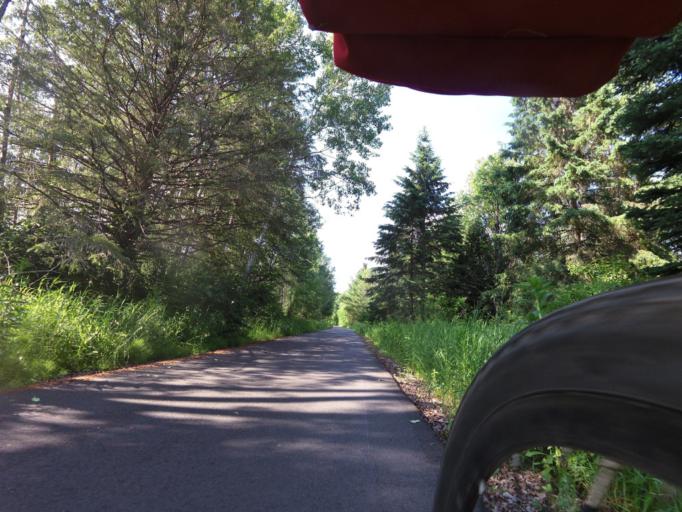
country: CA
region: Quebec
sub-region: Outaouais
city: Maniwaki
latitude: 46.2449
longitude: -76.0204
